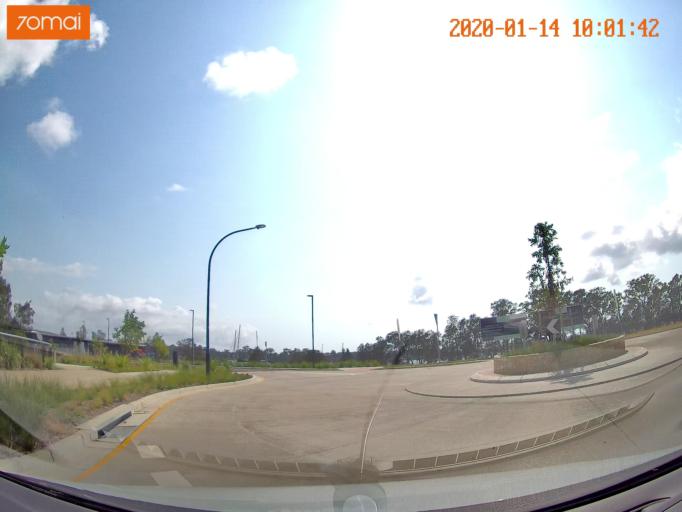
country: AU
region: New South Wales
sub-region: Wyong Shire
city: Kingfisher Shores
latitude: -33.1238
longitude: 151.5402
